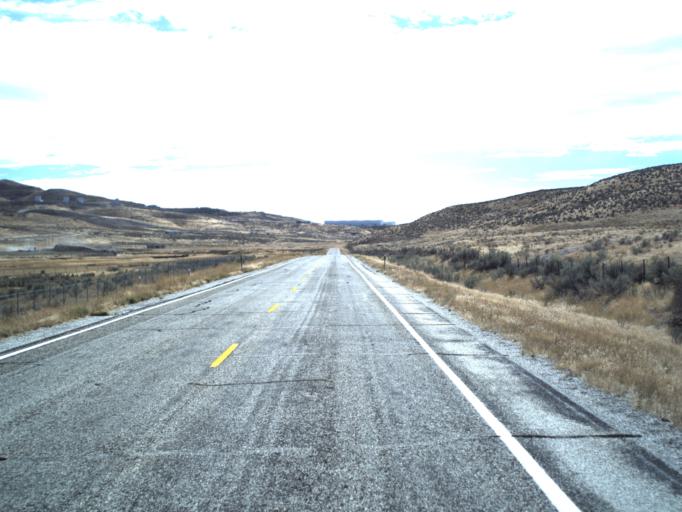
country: US
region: Utah
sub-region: Box Elder County
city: Tremonton
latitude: 41.7028
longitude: -112.4485
